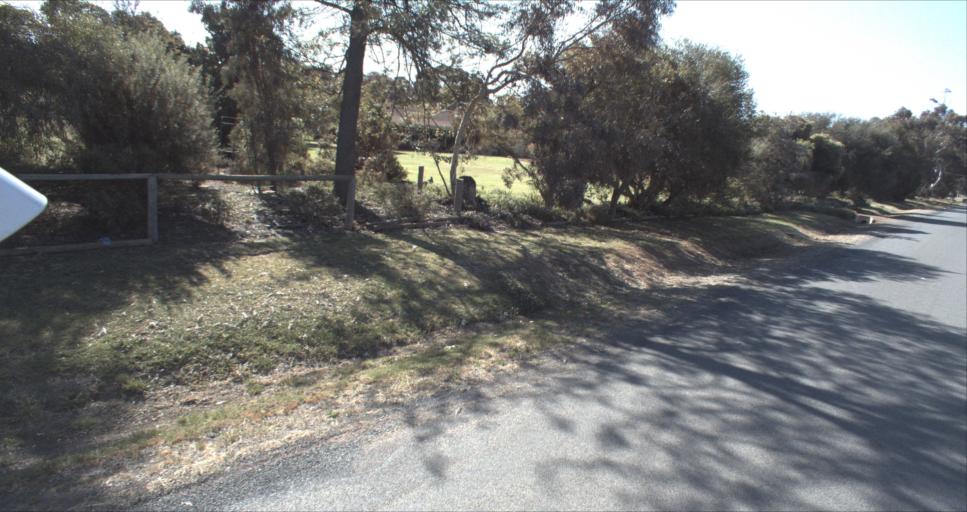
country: AU
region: New South Wales
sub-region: Leeton
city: Leeton
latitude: -34.5708
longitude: 146.4135
